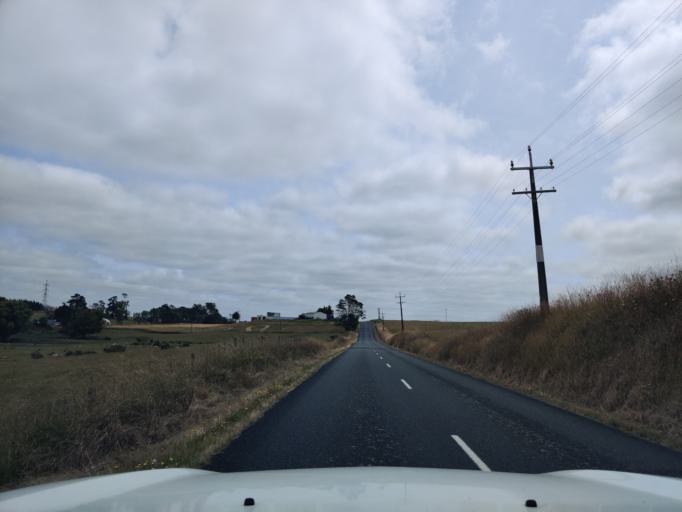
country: NZ
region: Waikato
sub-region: Waikato District
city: Te Kauwhata
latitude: -37.5098
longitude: 175.1805
